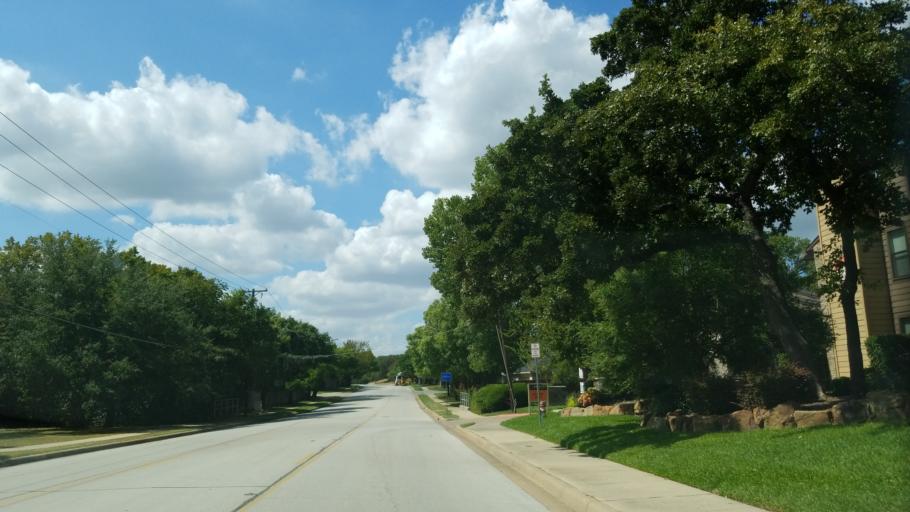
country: US
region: Texas
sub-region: Tarrant County
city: Grapevine
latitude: 32.9094
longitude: -97.1041
